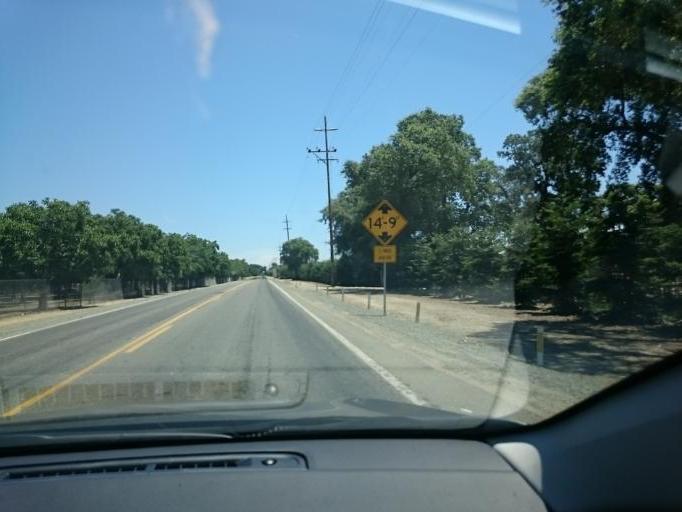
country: US
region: California
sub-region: San Joaquin County
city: Woodbridge
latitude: 38.1892
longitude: -121.3354
